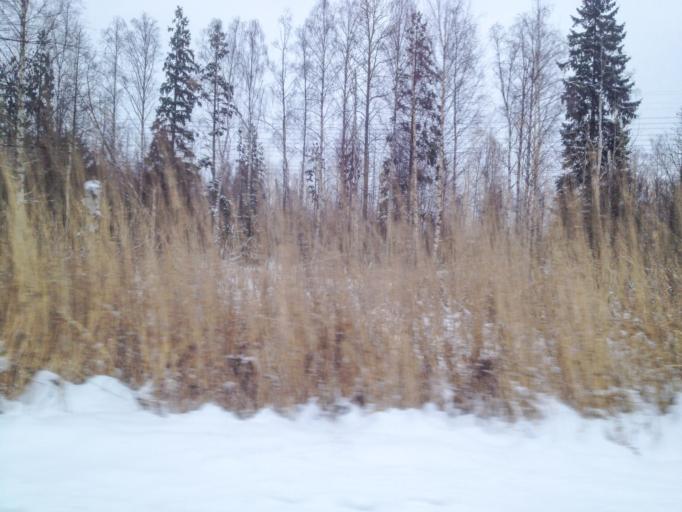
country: FI
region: Uusimaa
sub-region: Helsinki
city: Vantaa
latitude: 60.2197
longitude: 25.1564
